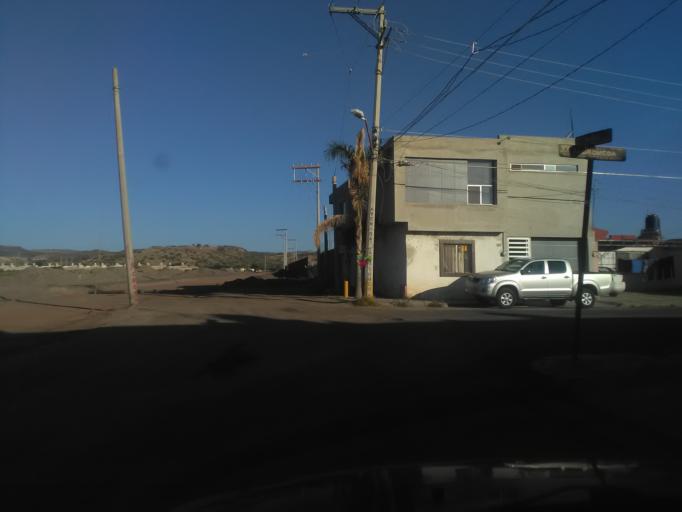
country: MX
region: Durango
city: Victoria de Durango
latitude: 23.9972
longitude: -104.7039
